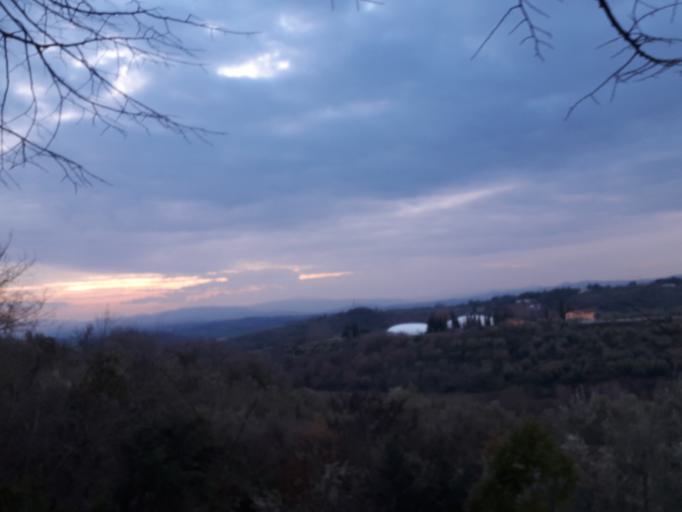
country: IT
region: Umbria
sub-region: Provincia di Perugia
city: Perugia
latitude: 43.0917
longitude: 12.3981
